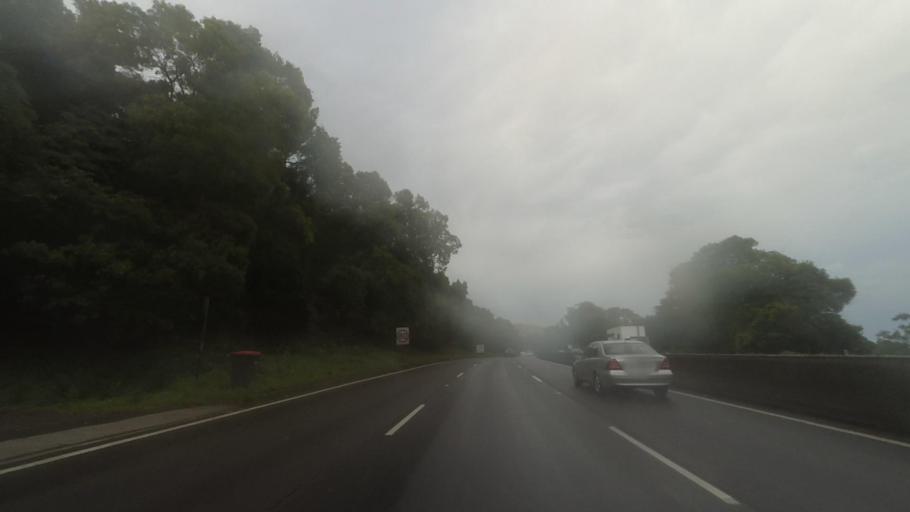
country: AU
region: New South Wales
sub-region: Wollongong
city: Mount Ousley
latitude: -34.3867
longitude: 150.8580
